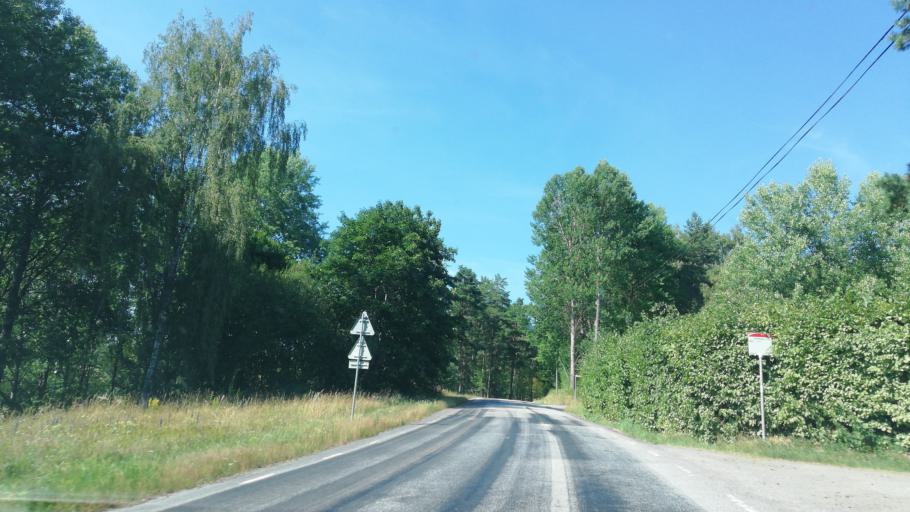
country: SE
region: OEstergoetland
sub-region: Finspangs Kommun
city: Finspang
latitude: 58.7251
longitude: 15.8319
